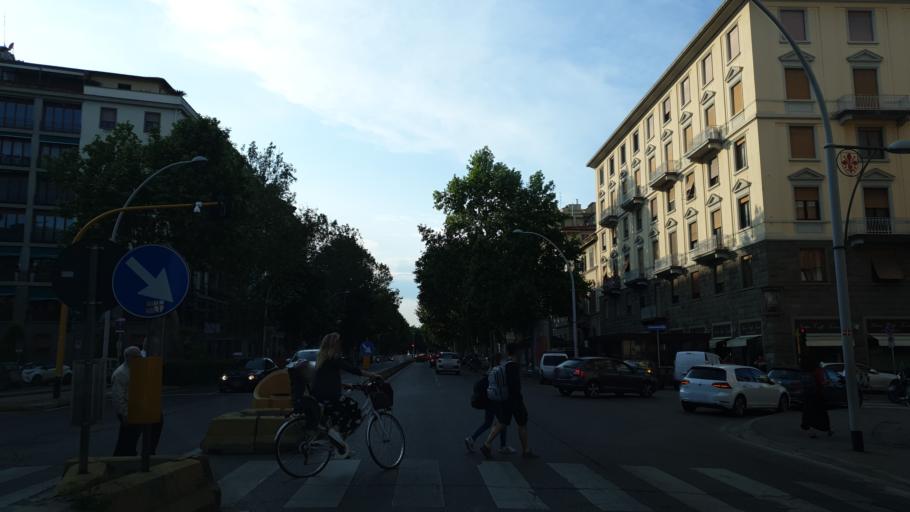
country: IT
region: Tuscany
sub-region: Province of Florence
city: Florence
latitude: 43.7802
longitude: 11.2655
